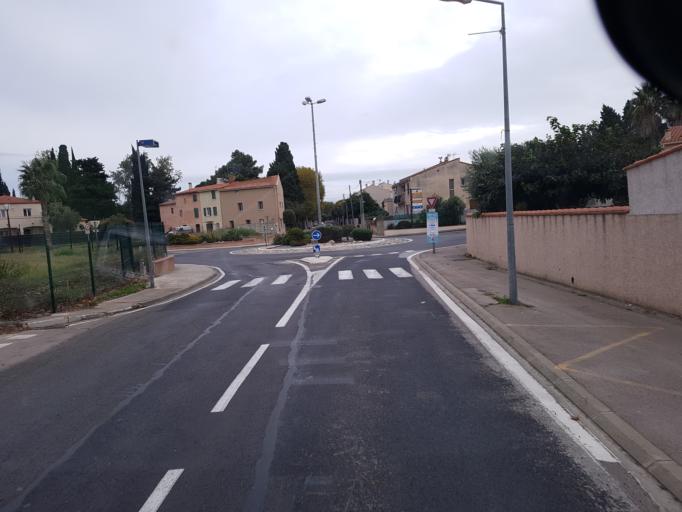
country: FR
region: Languedoc-Roussillon
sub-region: Departement des Pyrenees-Orientales
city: Torreilles
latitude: 42.7597
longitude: 2.9902
